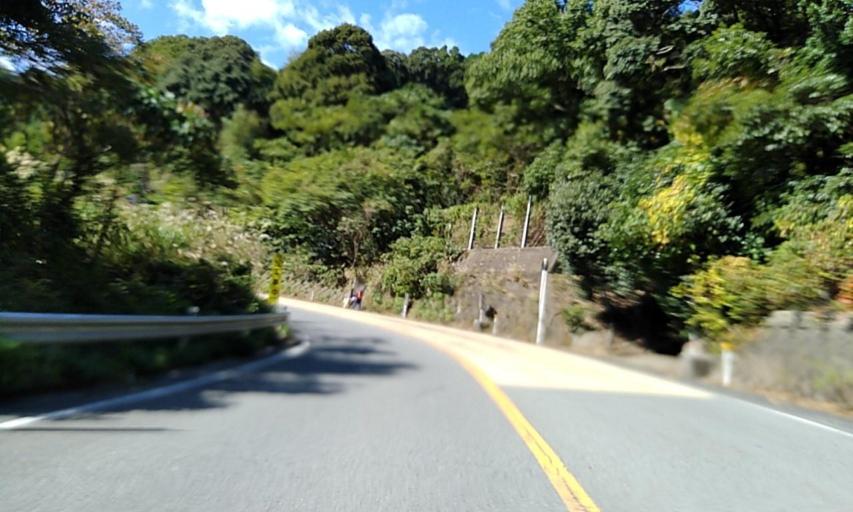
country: JP
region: Wakayama
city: Gobo
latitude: 33.9930
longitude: 135.1891
